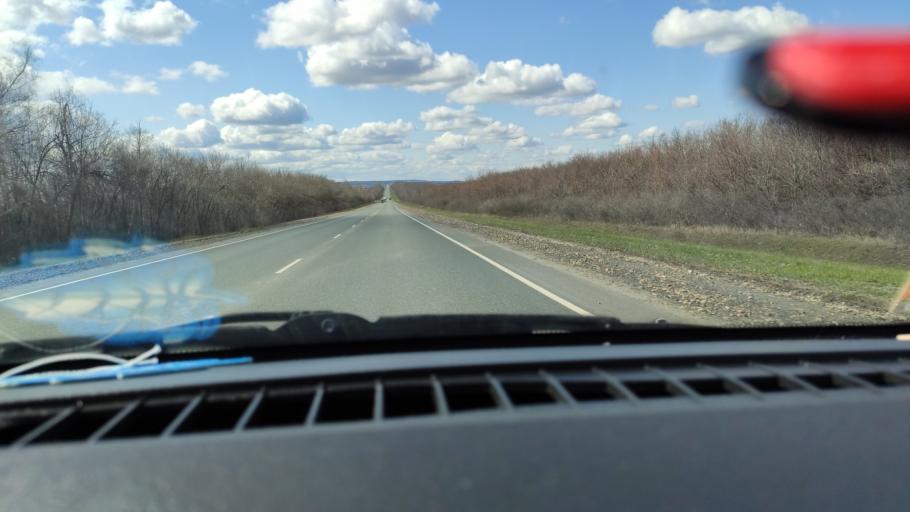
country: RU
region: Saratov
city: Khvalynsk
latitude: 52.6108
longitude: 48.1585
